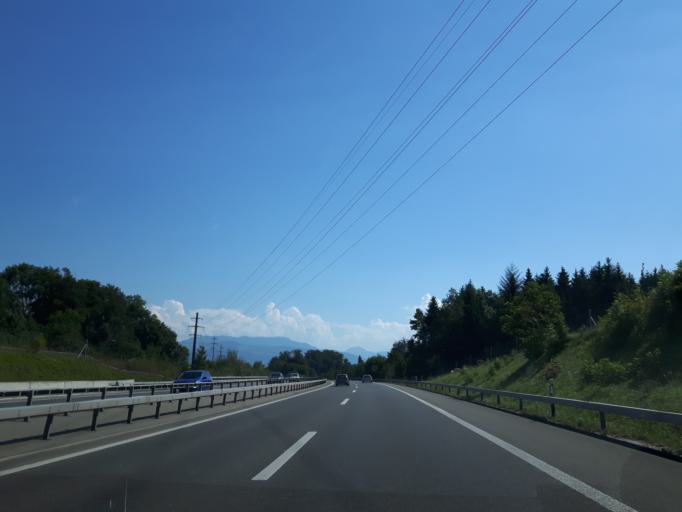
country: CH
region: Zurich
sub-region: Bezirk Affoltern
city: Knonau
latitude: 47.2330
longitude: 8.4581
